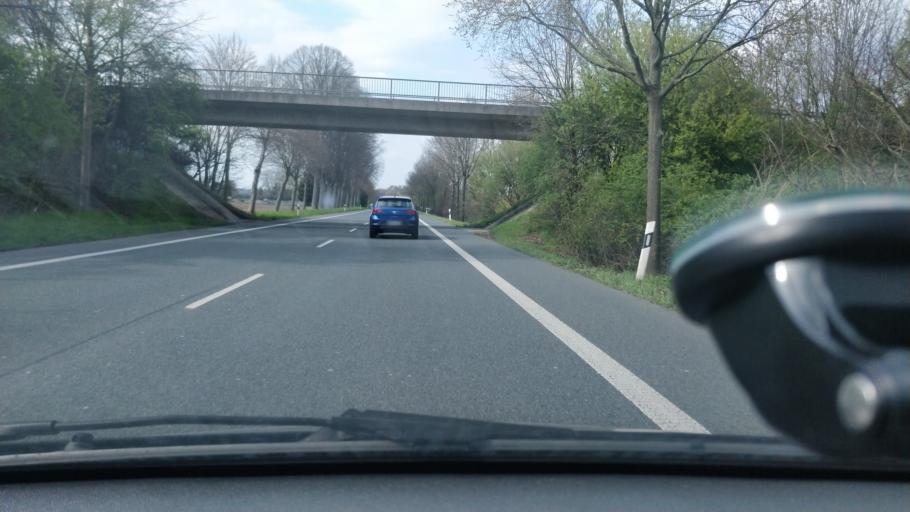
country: DE
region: North Rhine-Westphalia
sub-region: Regierungsbezirk Dusseldorf
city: Hamminkeln
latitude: 51.7530
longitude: 6.5889
